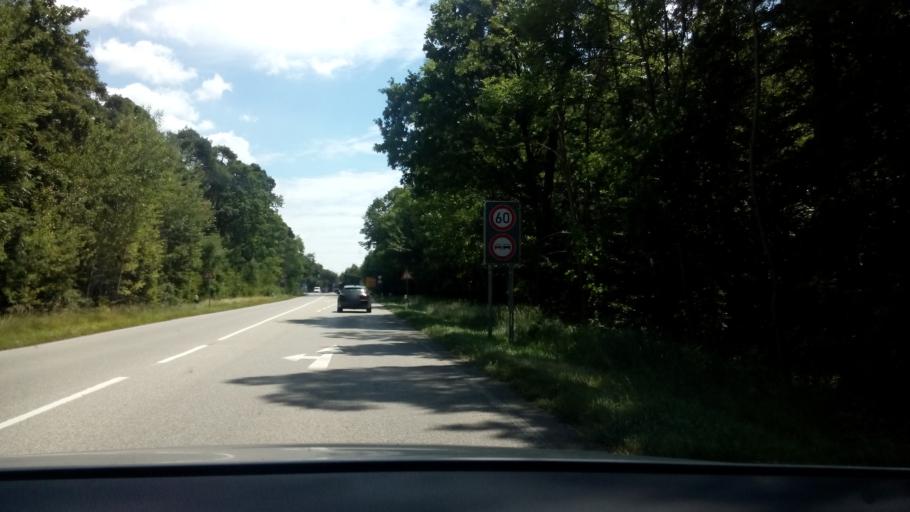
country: DE
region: Bavaria
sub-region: Upper Bavaria
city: Oberschleissheim
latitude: 48.2491
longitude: 11.5985
